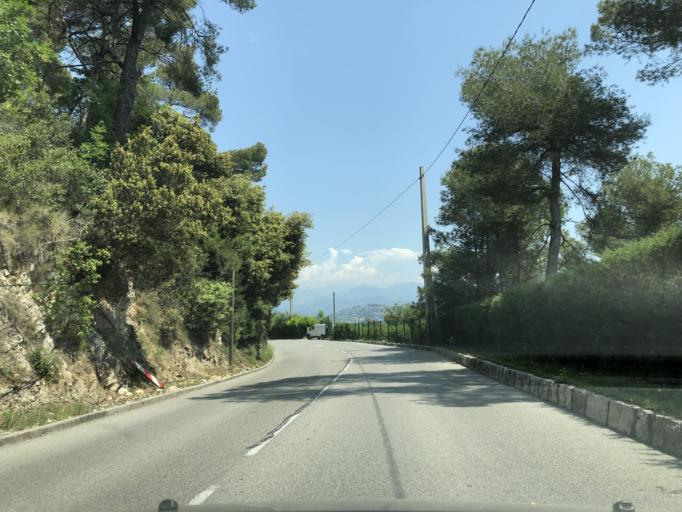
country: FR
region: Provence-Alpes-Cote d'Azur
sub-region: Departement des Alpes-Maritimes
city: Villefranche-sur-Mer
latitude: 43.7219
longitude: 7.3036
